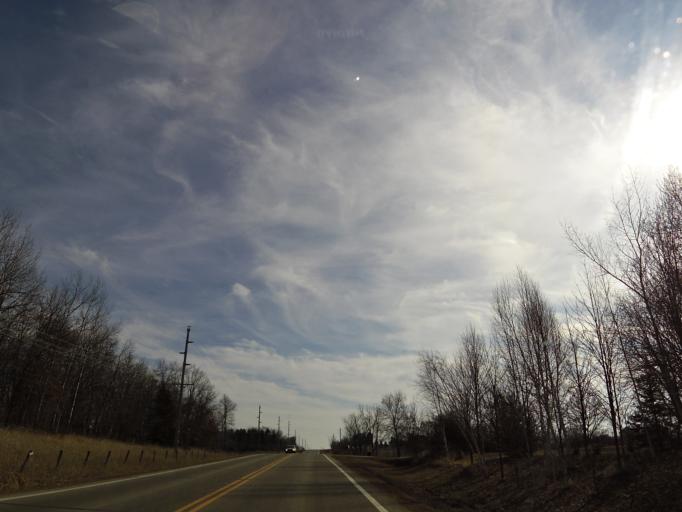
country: US
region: Minnesota
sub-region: Scott County
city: Prior Lake
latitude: 44.6248
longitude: -93.4403
